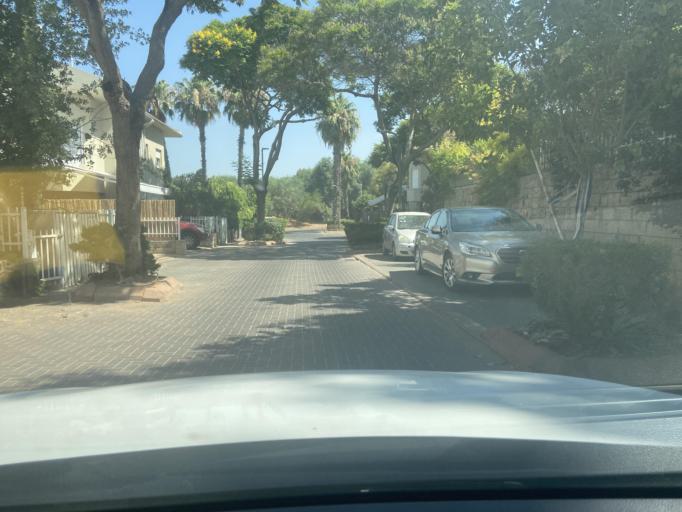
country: IL
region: Central District
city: Yehud
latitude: 32.0362
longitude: 34.8805
